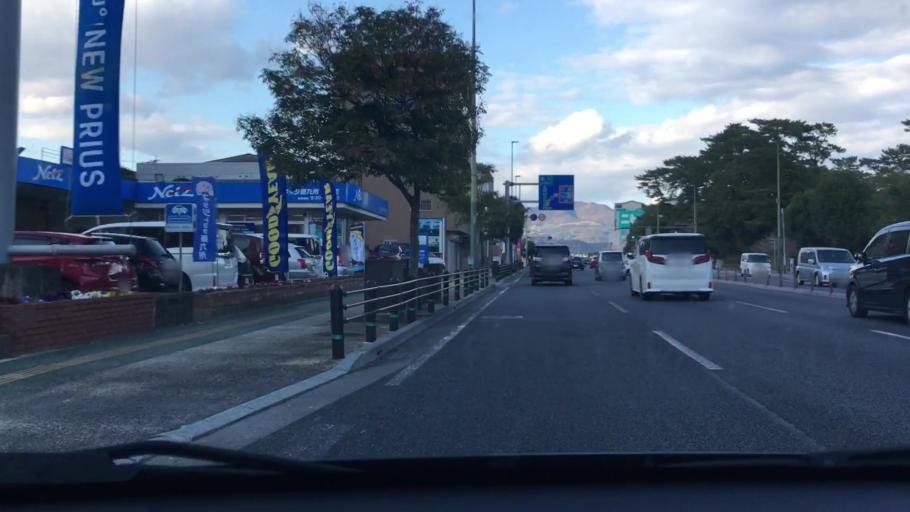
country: JP
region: Oita
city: Beppu
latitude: 33.3133
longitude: 131.5007
